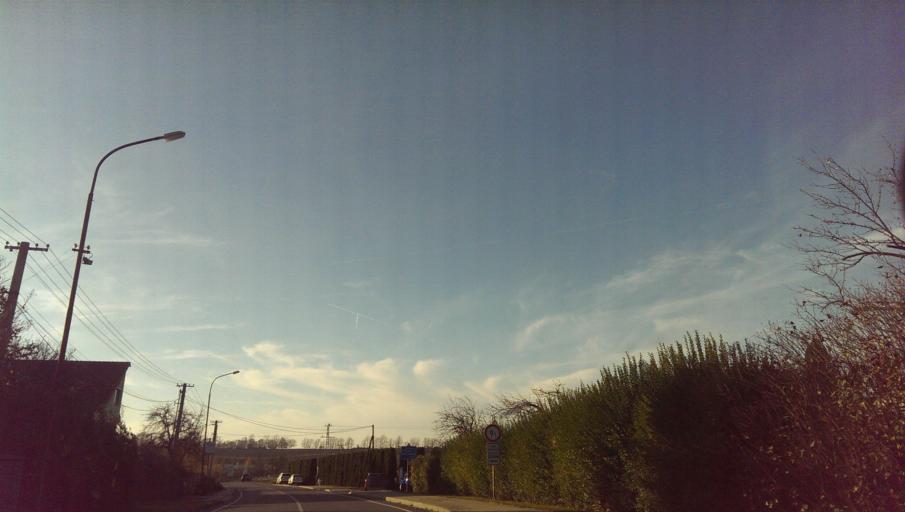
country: CZ
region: South Moravian
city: Louka
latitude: 48.9168
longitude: 17.4837
